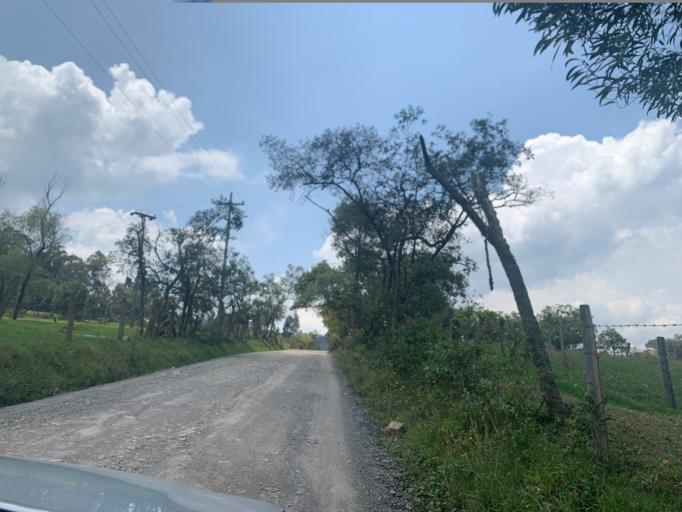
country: CO
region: Boyaca
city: Chiquinquira
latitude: 5.6031
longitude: -73.7660
